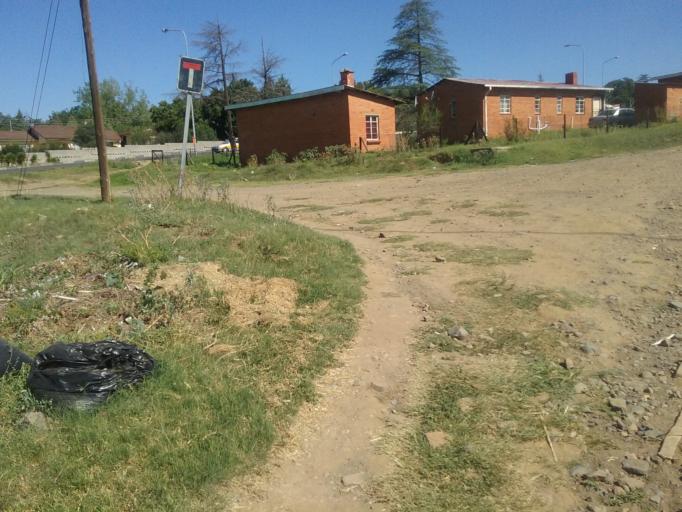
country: LS
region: Maseru
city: Maseru
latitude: -29.3022
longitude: 27.4676
